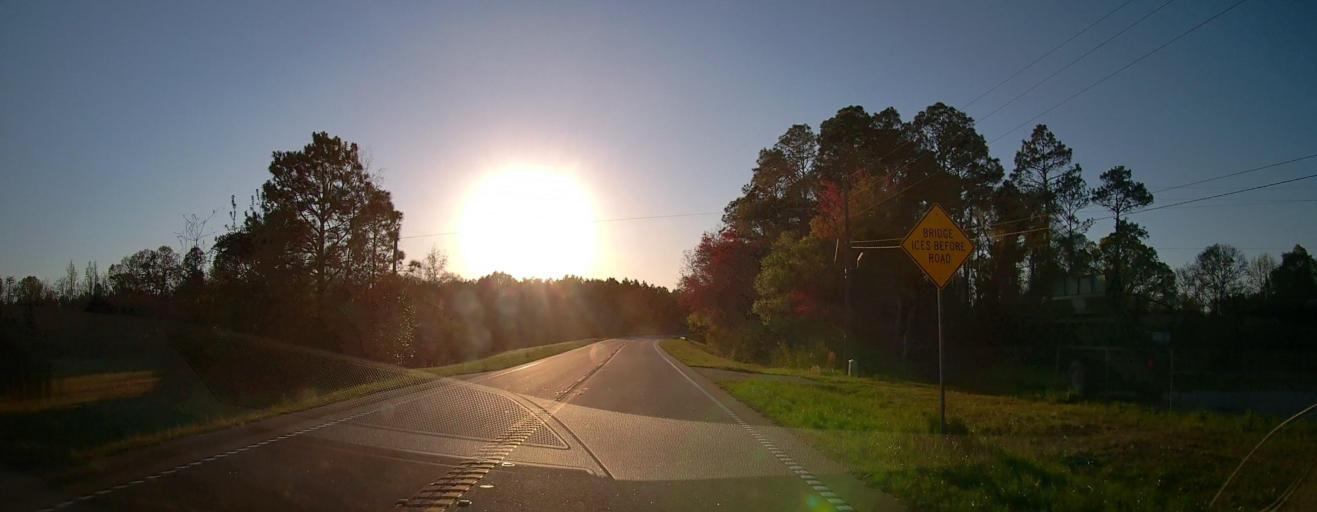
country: US
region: Georgia
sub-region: Wilcox County
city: Rochelle
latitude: 31.9448
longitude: -83.5507
